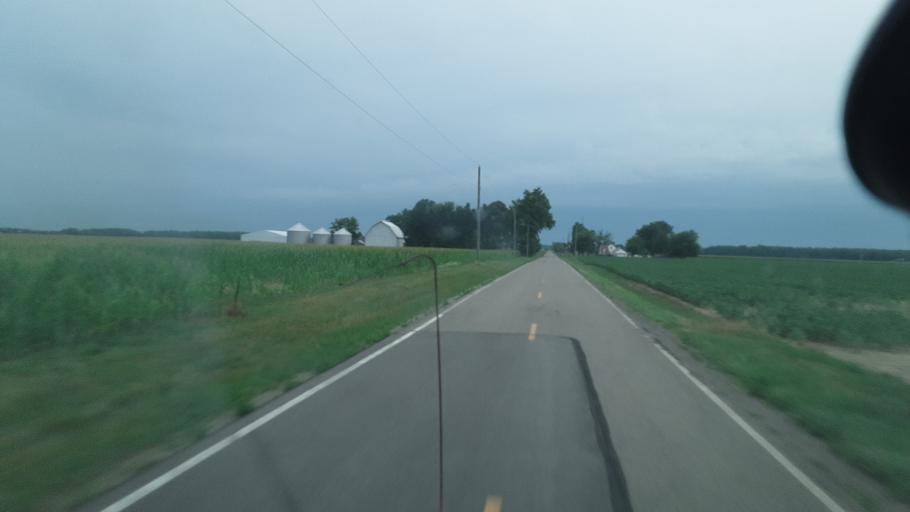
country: US
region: Ohio
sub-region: Defiance County
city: Hicksville
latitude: 41.2670
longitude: -84.7421
